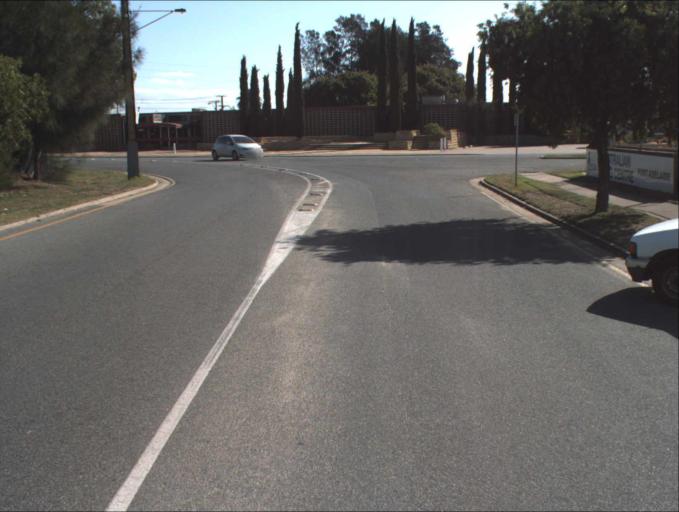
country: AU
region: South Australia
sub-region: Port Adelaide Enfield
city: Alberton
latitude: -34.8499
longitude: 138.5390
